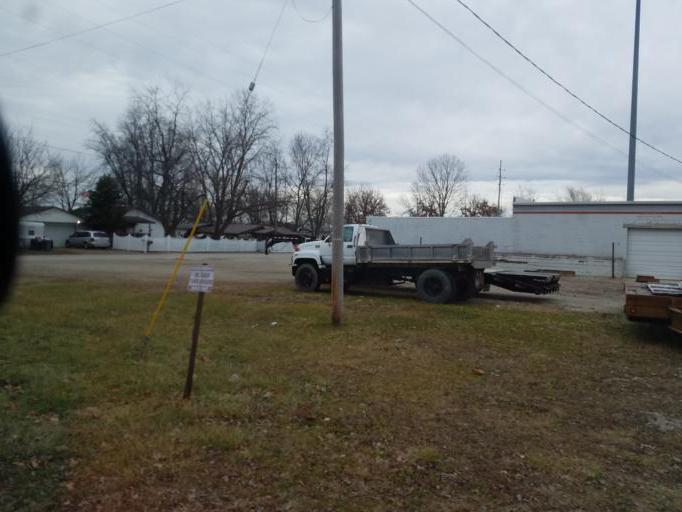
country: US
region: Ohio
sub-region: Marion County
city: Marion
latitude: 40.5959
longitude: -83.1068
